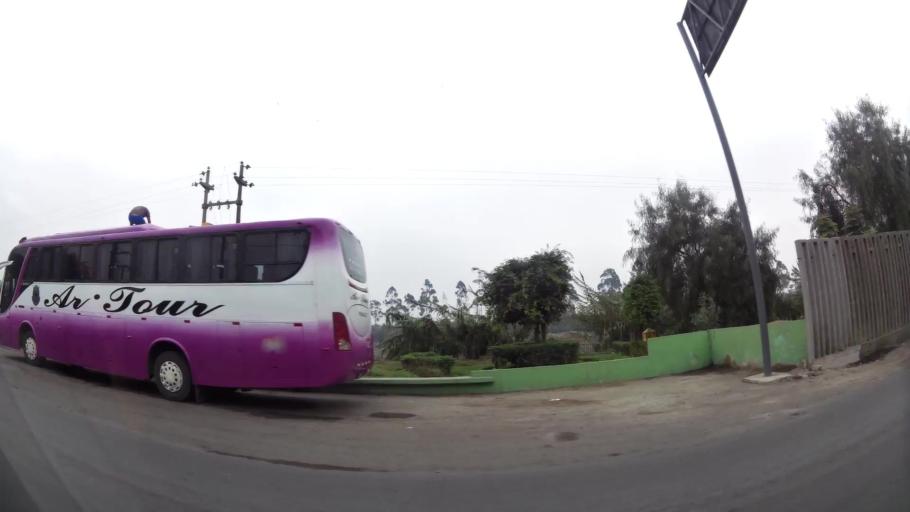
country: PE
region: Lima
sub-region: Lima
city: Vitarte
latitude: -12.0198
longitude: -76.9472
